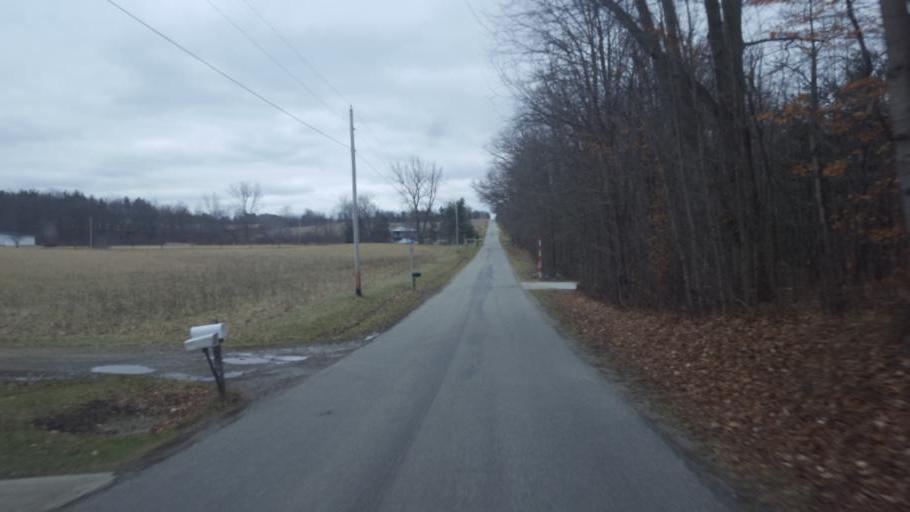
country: US
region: Ohio
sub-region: Crawford County
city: Crestline
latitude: 40.7255
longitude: -82.6891
